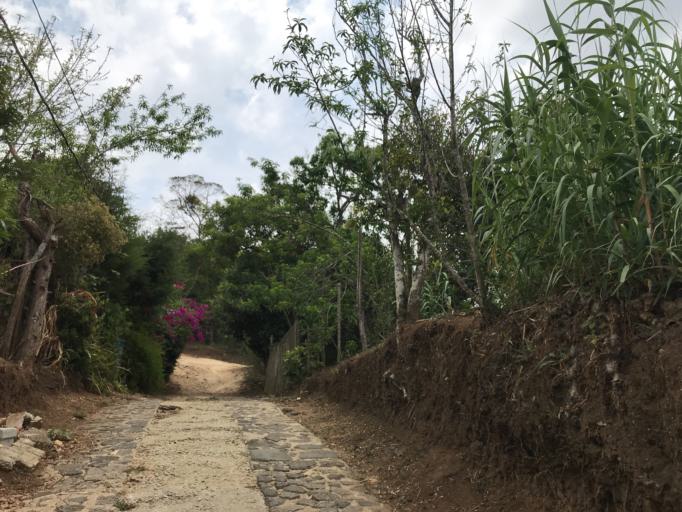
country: GT
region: Guatemala
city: Santa Catarina Pinula
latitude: 14.5415
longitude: -90.4897
